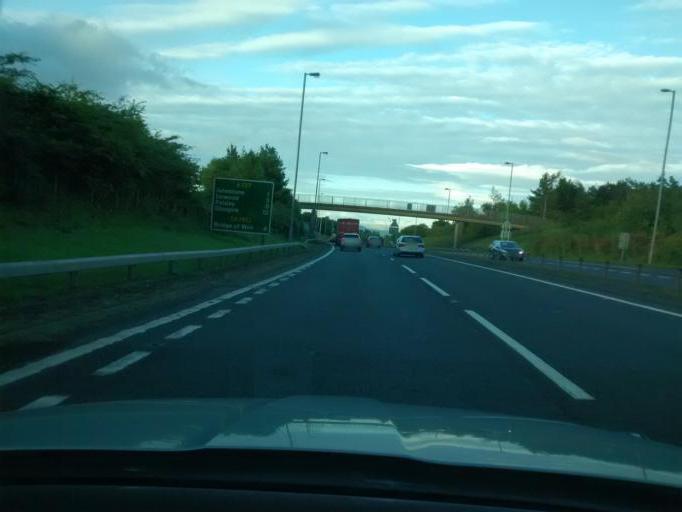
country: GB
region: Scotland
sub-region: Renfrewshire
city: Johnstone
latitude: 55.8344
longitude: -4.5286
